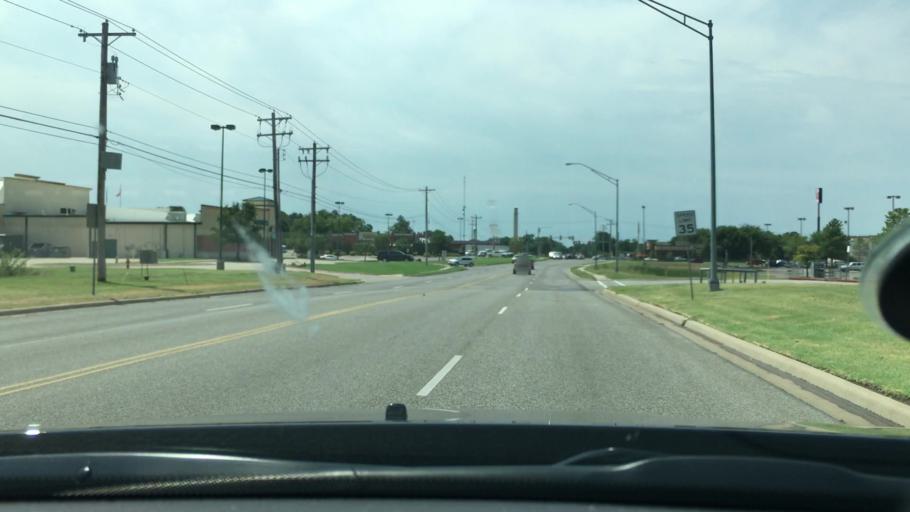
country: US
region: Oklahoma
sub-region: Carter County
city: Ardmore
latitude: 34.1902
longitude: -97.1605
